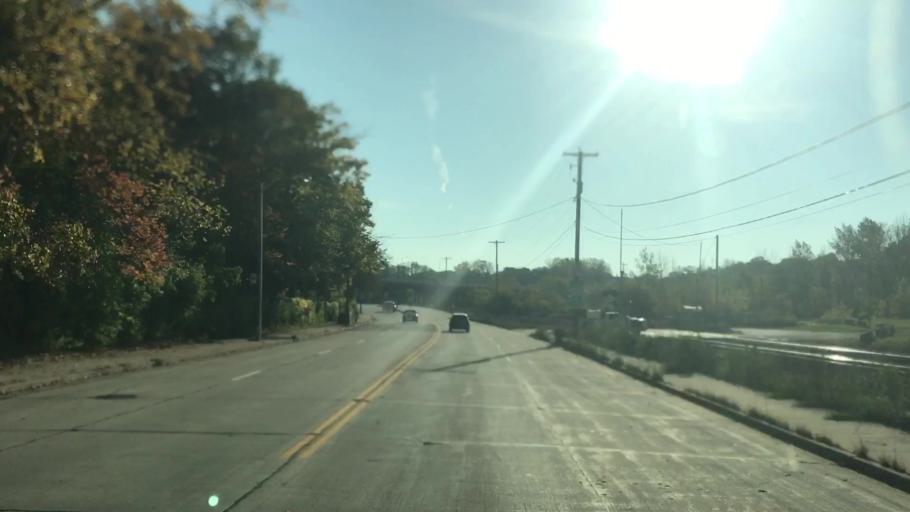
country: US
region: Wisconsin
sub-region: Milwaukee County
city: Wauwatosa
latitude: 43.0438
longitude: -87.9870
